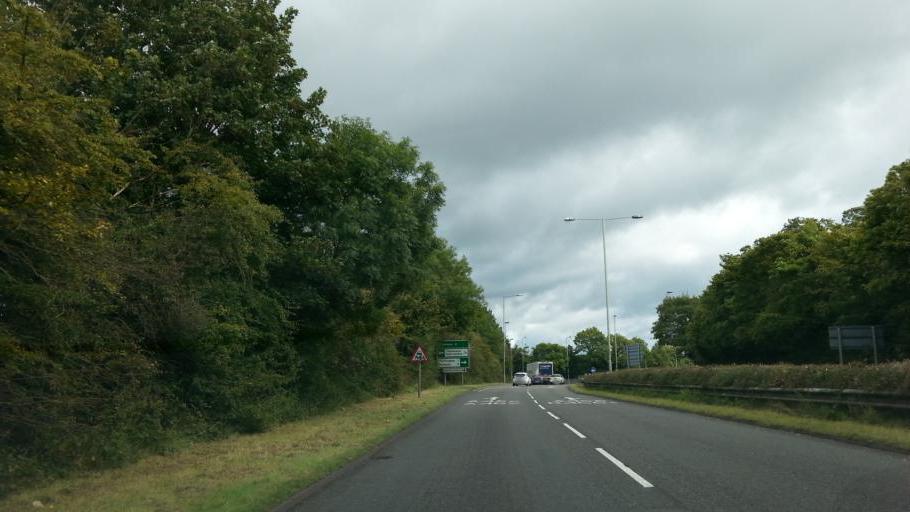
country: GB
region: England
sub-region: Dudley
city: Halesowen
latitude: 52.4435
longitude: -2.0465
